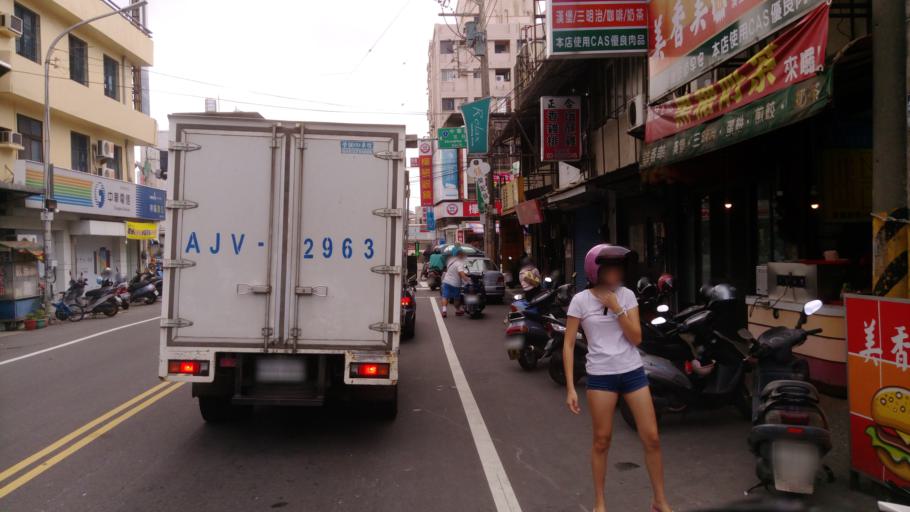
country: TW
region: Taiwan
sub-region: Hsinchu
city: Hsinchu
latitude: 24.7888
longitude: 120.9284
